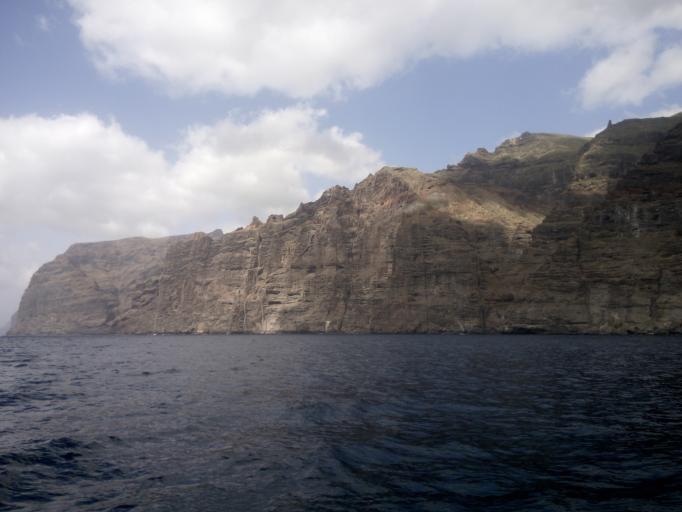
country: ES
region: Canary Islands
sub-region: Provincia de Santa Cruz de Tenerife
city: Santiago del Teide
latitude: 28.2513
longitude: -16.8417
